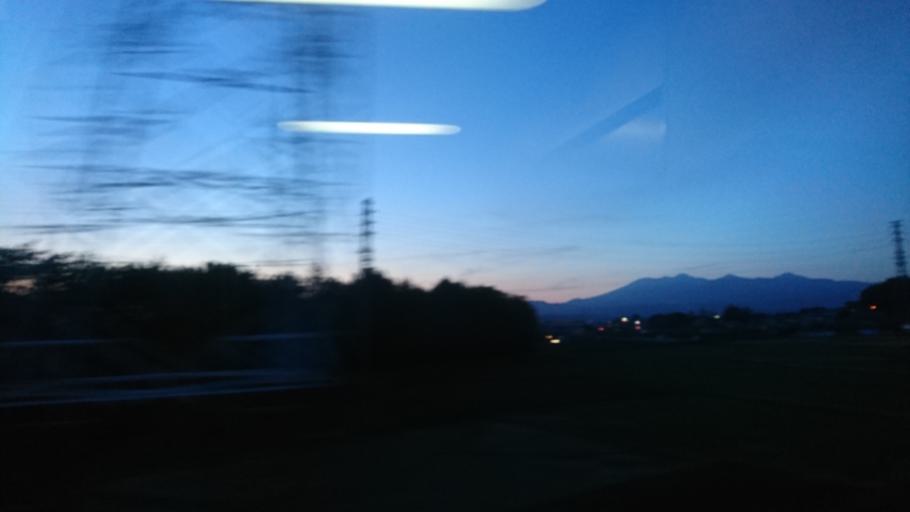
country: JP
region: Tochigi
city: Yaita
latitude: 36.7912
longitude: 139.9542
